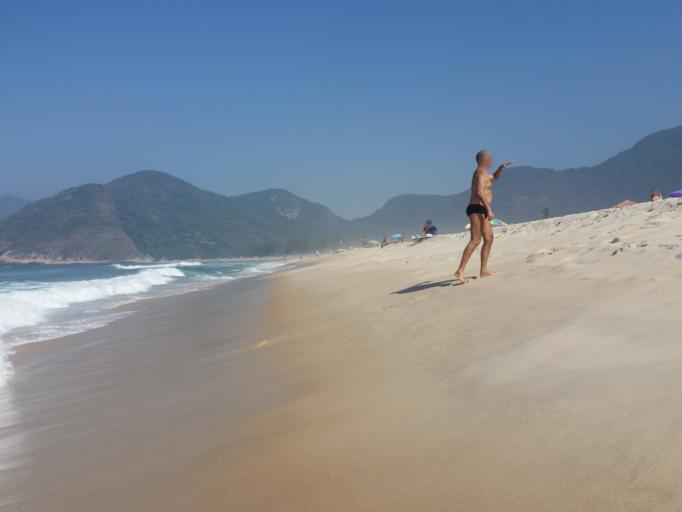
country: BR
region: Rio de Janeiro
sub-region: Nilopolis
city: Nilopolis
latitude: -23.0490
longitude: -43.5268
